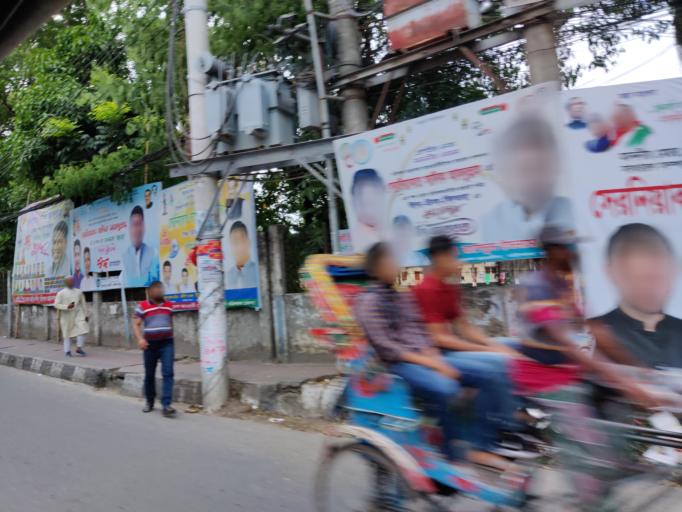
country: BD
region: Barisal
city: Barisal
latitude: 22.7068
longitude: 90.3710
